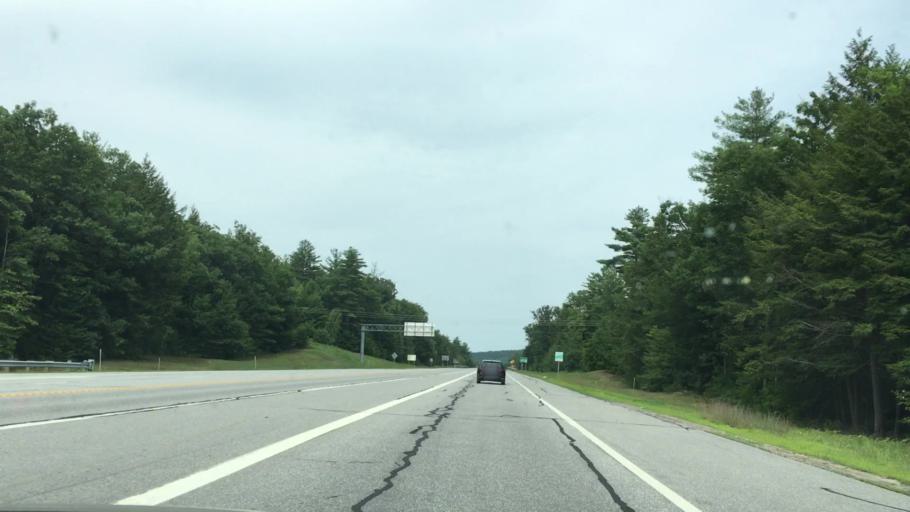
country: US
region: New Hampshire
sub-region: Hillsborough County
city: Hillsborough
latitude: 43.1176
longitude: -71.9119
